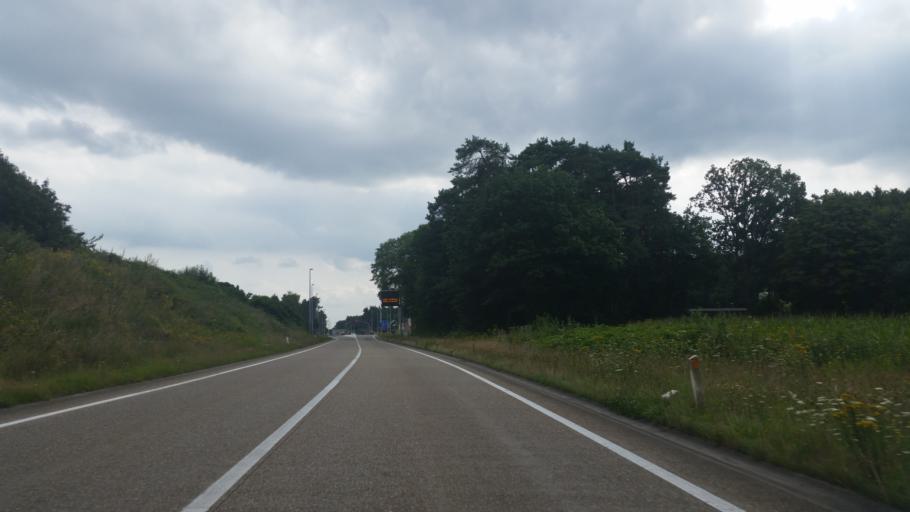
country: BE
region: Flanders
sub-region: Provincie Antwerpen
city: Kasterlee
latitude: 51.2424
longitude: 4.9551
